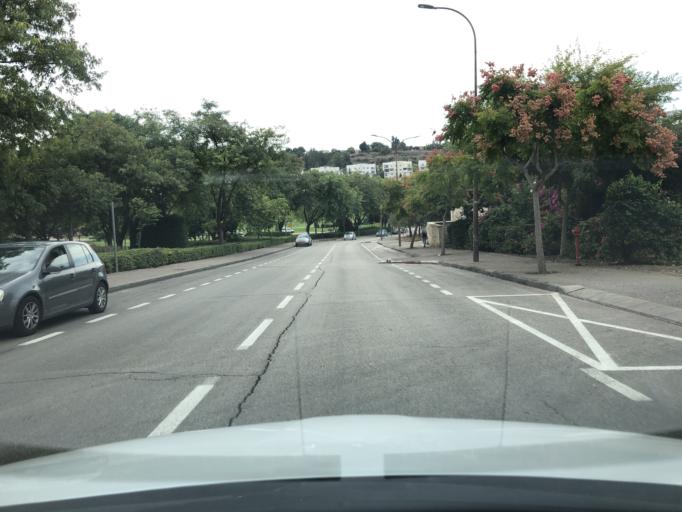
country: IL
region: Central District
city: Modiin
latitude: 31.8986
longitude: 35.0159
